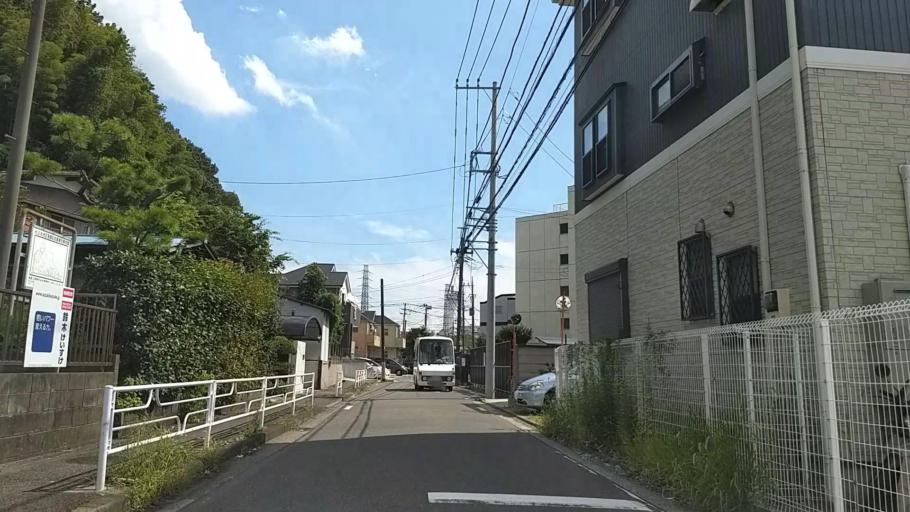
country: JP
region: Kanagawa
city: Yokohama
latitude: 35.5200
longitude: 139.5802
